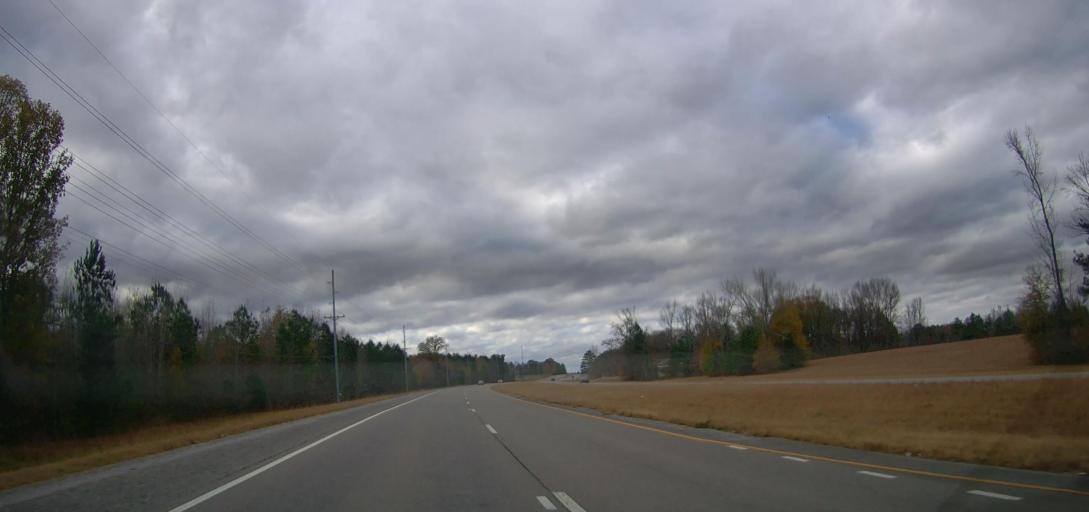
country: US
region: Alabama
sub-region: Lawrence County
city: Town Creek
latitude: 34.5739
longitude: -87.3979
